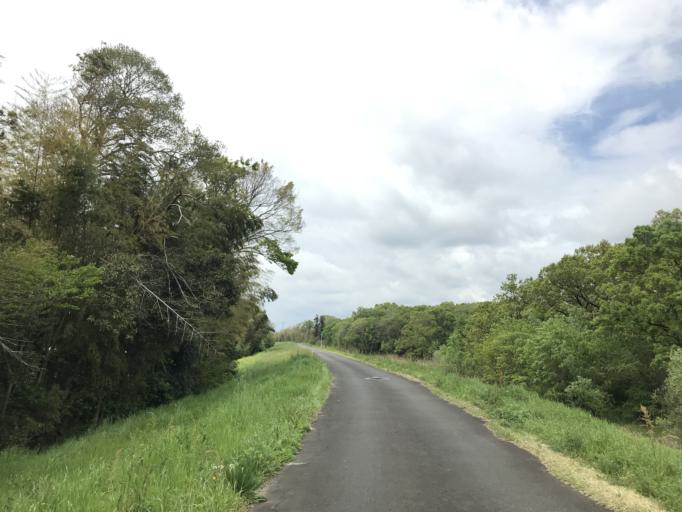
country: JP
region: Ibaraki
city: Moriya
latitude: 35.9727
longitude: 140.0025
